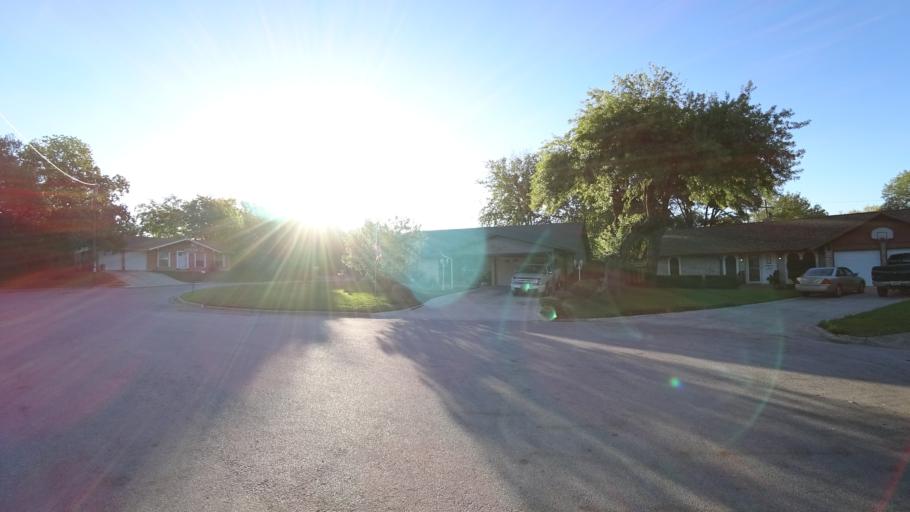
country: US
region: Texas
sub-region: Travis County
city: Austin
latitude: 30.3001
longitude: -97.6803
